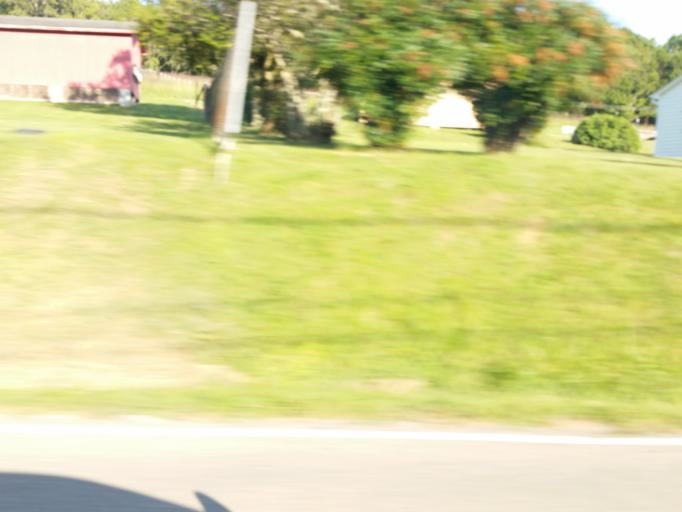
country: US
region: Tennessee
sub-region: Union County
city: Condon
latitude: 36.1829
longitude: -83.8135
